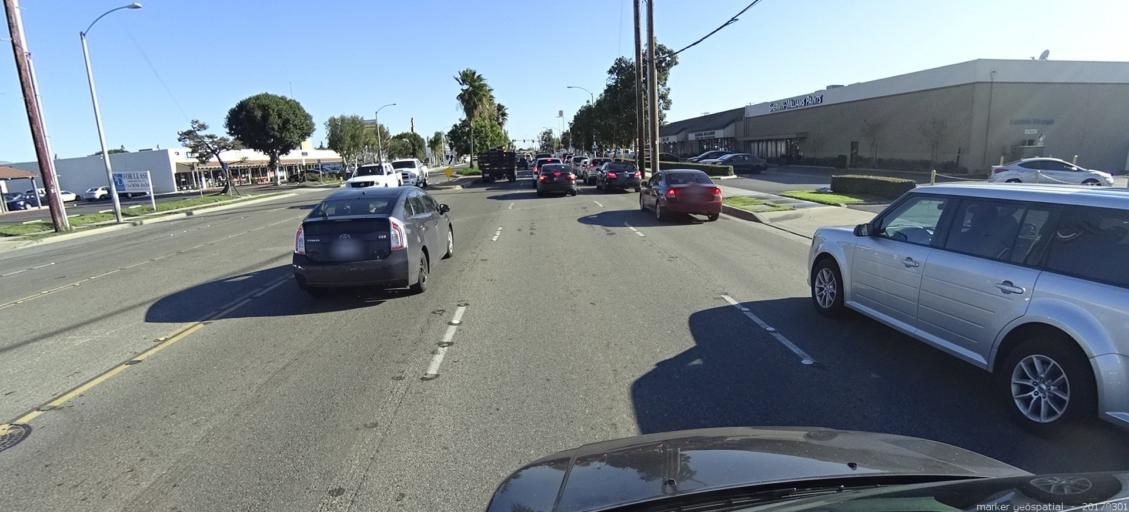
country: US
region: California
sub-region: Orange County
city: Placentia
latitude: 33.8529
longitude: -117.8580
